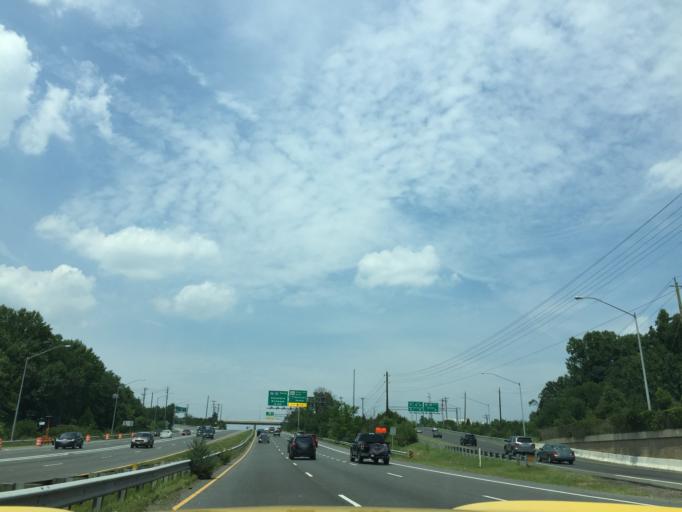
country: US
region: Maryland
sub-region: Prince George's County
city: Oxon Hill
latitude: 38.7953
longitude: -76.9986
